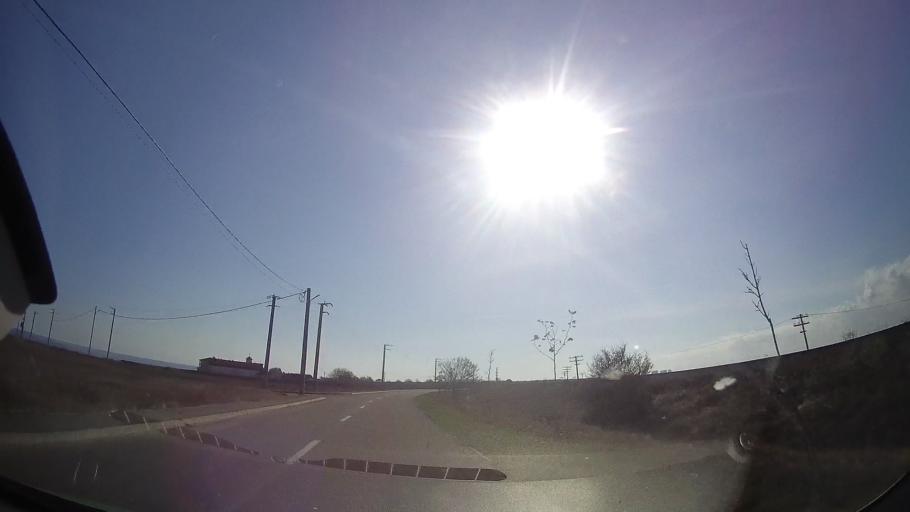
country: RO
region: Constanta
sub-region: Comuna Costinesti
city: Schitu
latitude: 43.9261
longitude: 28.6326
